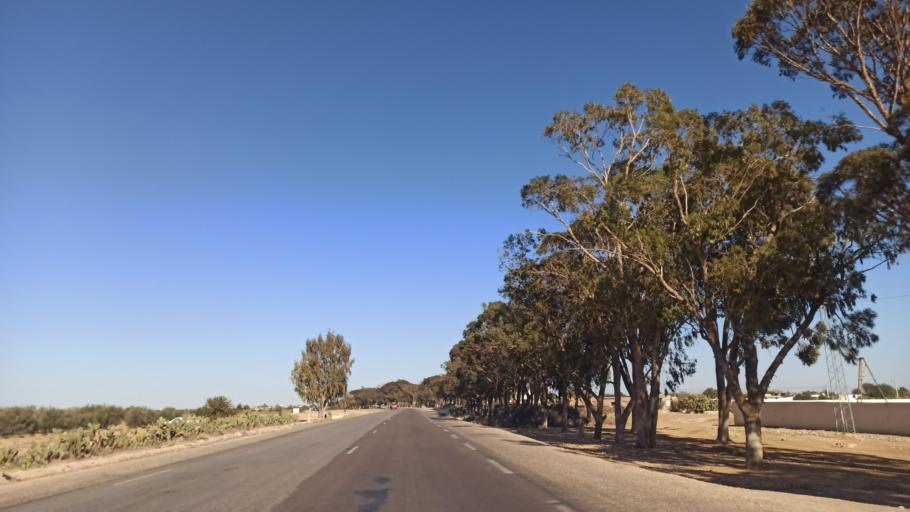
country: TN
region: Sidi Bu Zayd
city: Jilma
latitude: 35.2445
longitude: 9.3935
